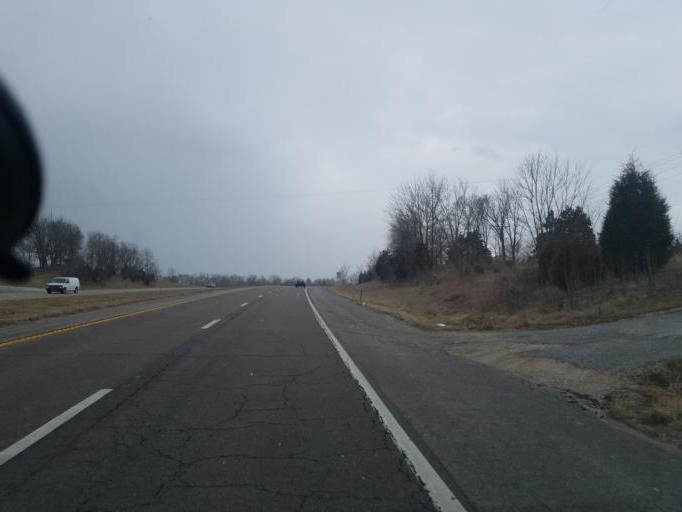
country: US
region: Missouri
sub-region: Boone County
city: Hallsville
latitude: 39.1178
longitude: -92.3297
